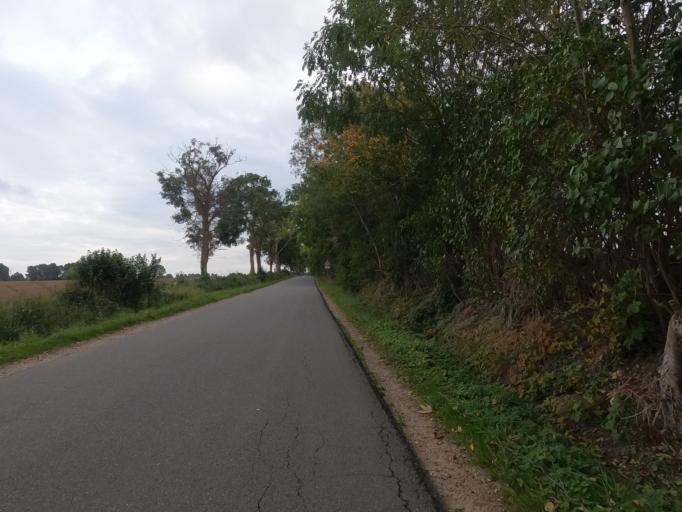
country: DE
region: Schleswig-Holstein
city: Neukirchen
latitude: 54.3186
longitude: 11.0370
